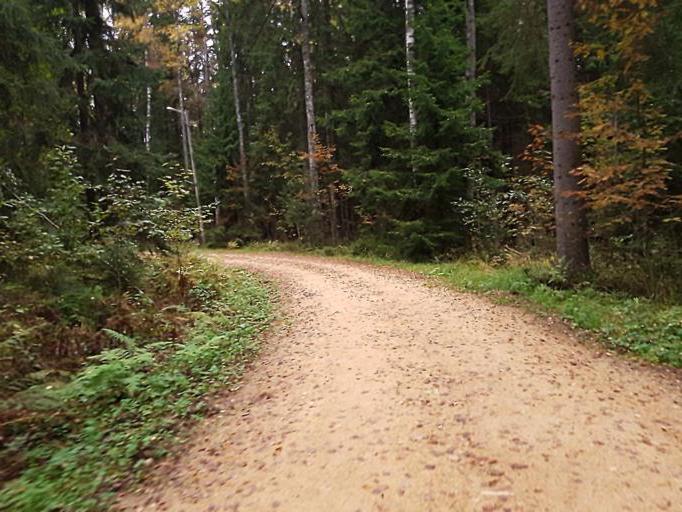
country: FI
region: Uusimaa
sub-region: Helsinki
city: Helsinki
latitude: 60.2635
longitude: 24.9142
